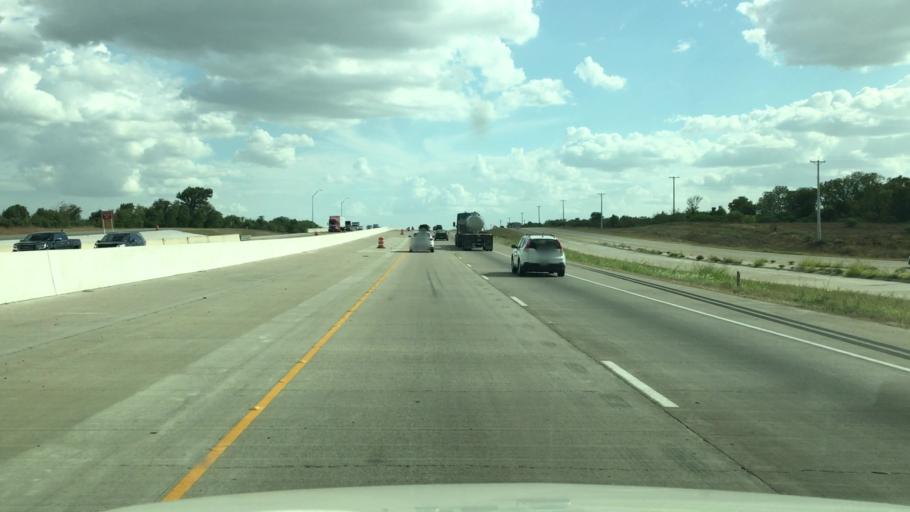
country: US
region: Texas
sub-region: McLennan County
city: Bruceville-Eddy
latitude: 31.2640
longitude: -97.2710
